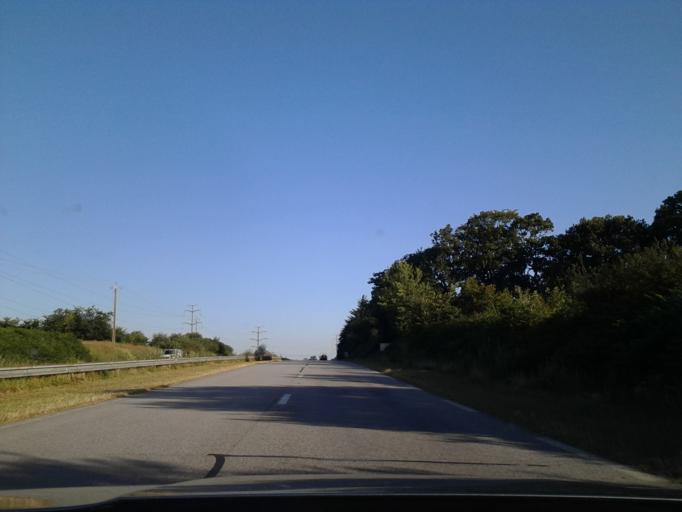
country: FR
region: Lower Normandy
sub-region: Departement de la Manche
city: La Glacerie
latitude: 49.5815
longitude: -1.5880
